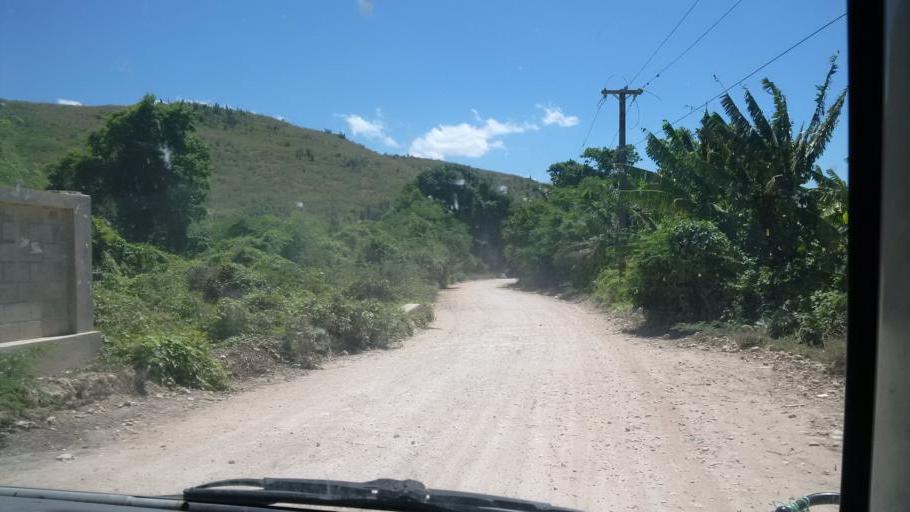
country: HT
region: Ouest
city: Thomazeau
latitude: 18.6569
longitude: -72.1354
